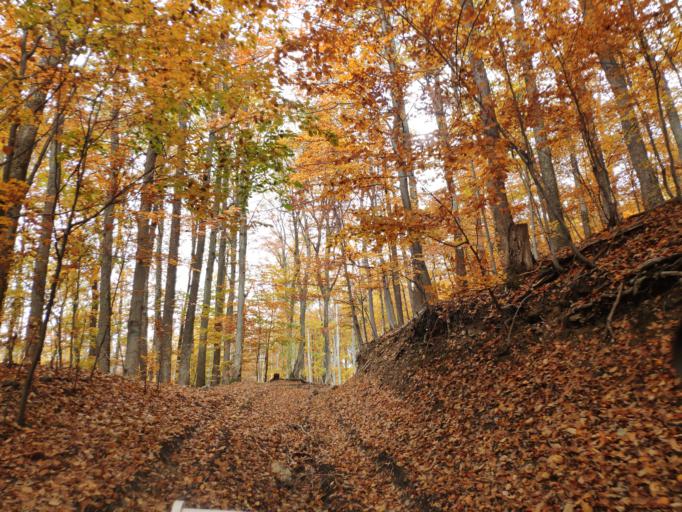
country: SK
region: Kosicky
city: Medzev
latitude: 48.7341
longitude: 20.9875
